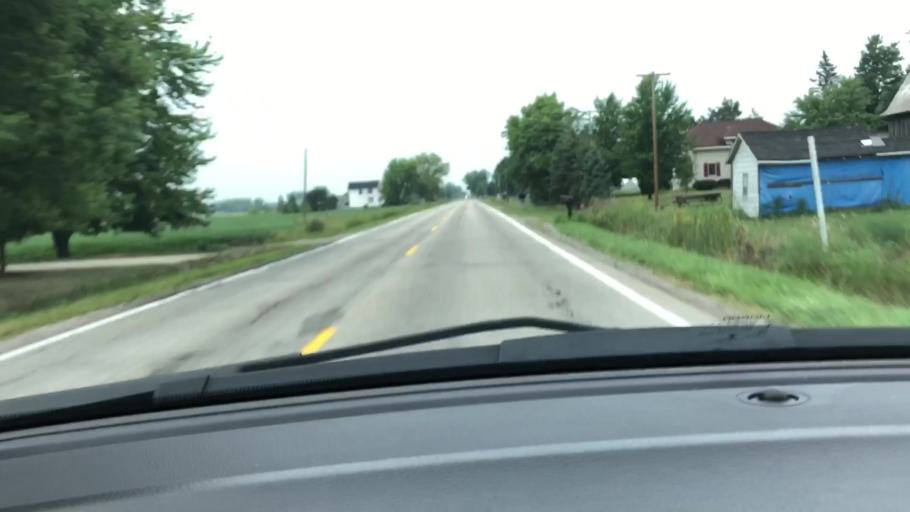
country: US
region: Michigan
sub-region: Bay County
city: Auburn
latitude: 43.5711
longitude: -84.0897
